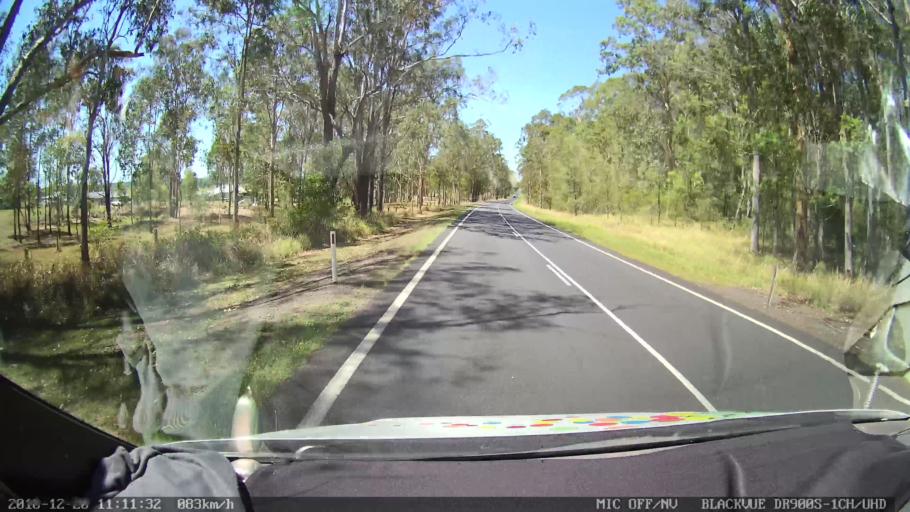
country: AU
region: New South Wales
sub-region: Richmond Valley
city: Casino
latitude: -28.9622
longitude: 153.0134
